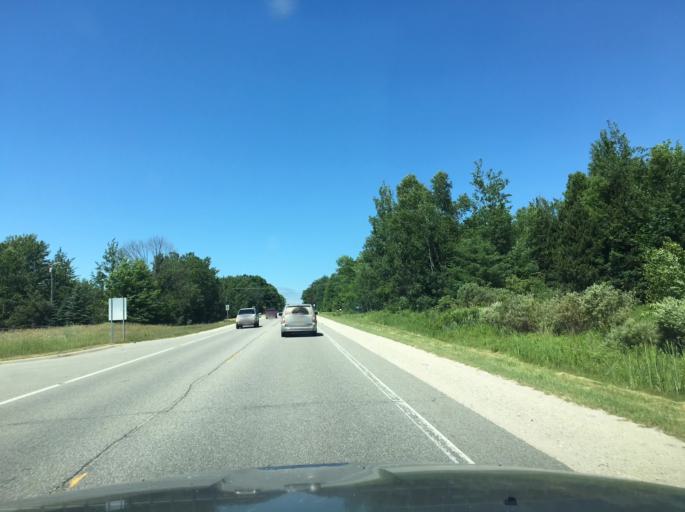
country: US
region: Michigan
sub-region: Osceola County
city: Reed City
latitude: 43.8876
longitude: -85.5600
